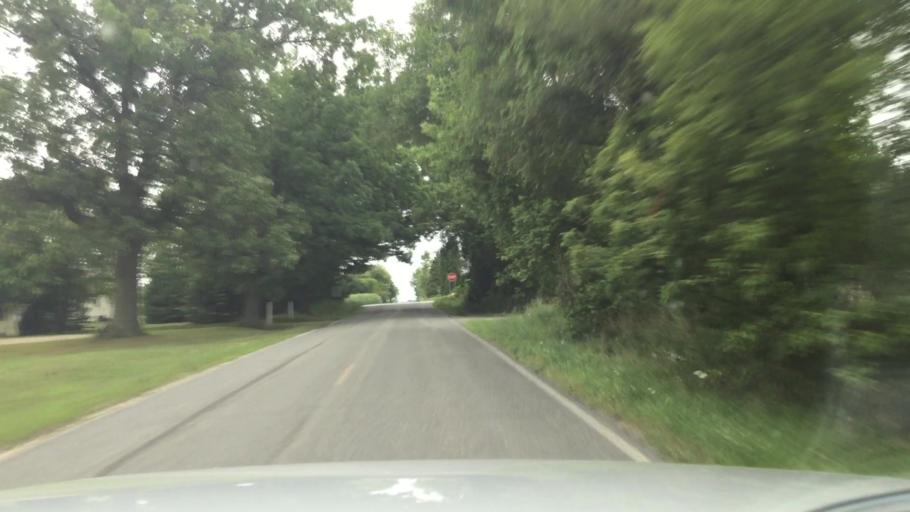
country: US
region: Michigan
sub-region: Montcalm County
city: Greenville
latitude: 43.1913
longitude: -85.2231
